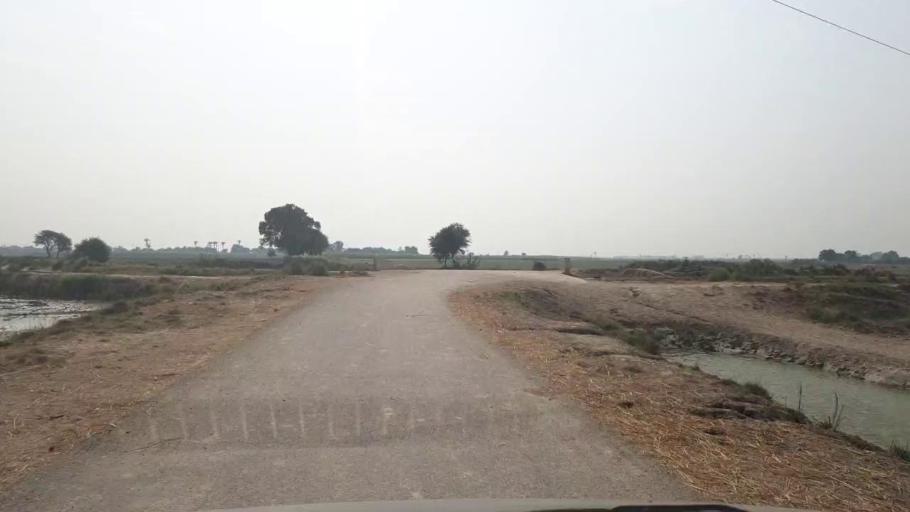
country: PK
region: Sindh
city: Tando Muhammad Khan
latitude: 25.1111
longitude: 68.3851
